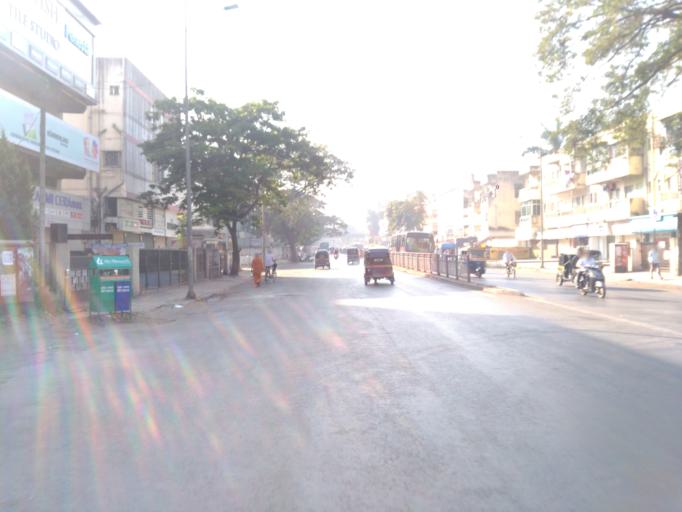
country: IN
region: Maharashtra
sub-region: Pune Division
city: Pune
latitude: 18.5038
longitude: 73.8688
